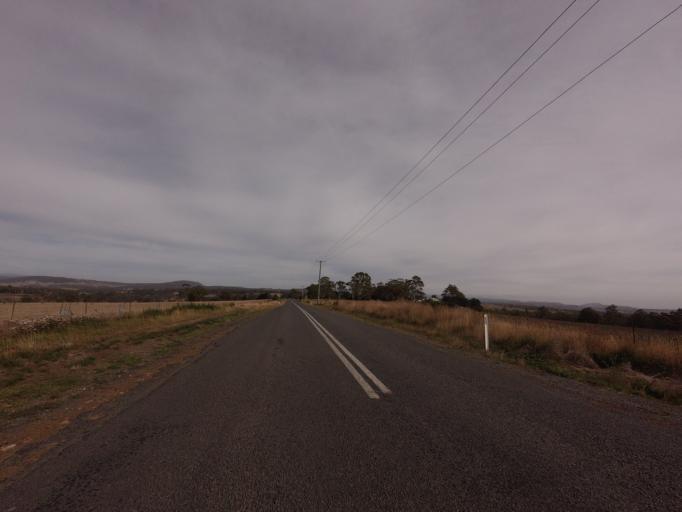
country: AU
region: Tasmania
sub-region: Brighton
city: Bridgewater
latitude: -42.3991
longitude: 147.4425
